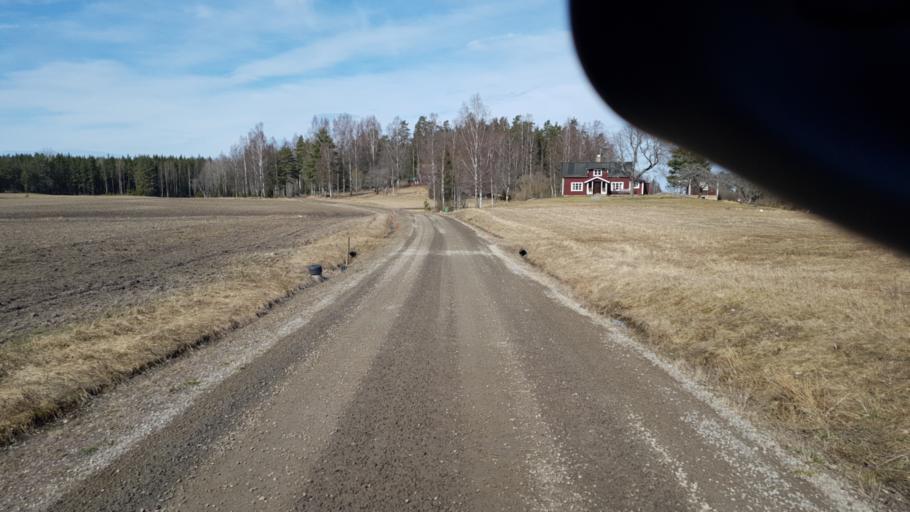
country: SE
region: Vaermland
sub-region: Grums Kommun
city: Grums
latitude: 59.5273
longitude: 12.9191
